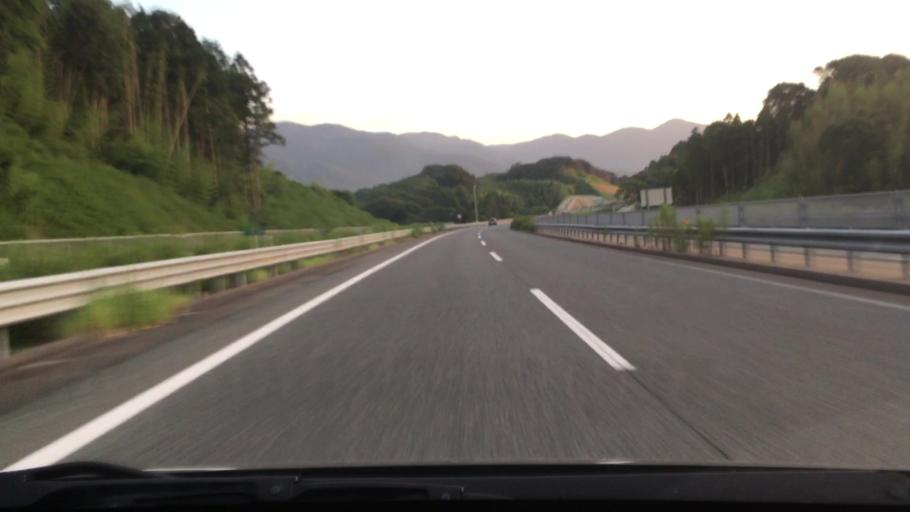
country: JP
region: Fukuoka
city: Maebaru-chuo
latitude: 33.5365
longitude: 130.1954
